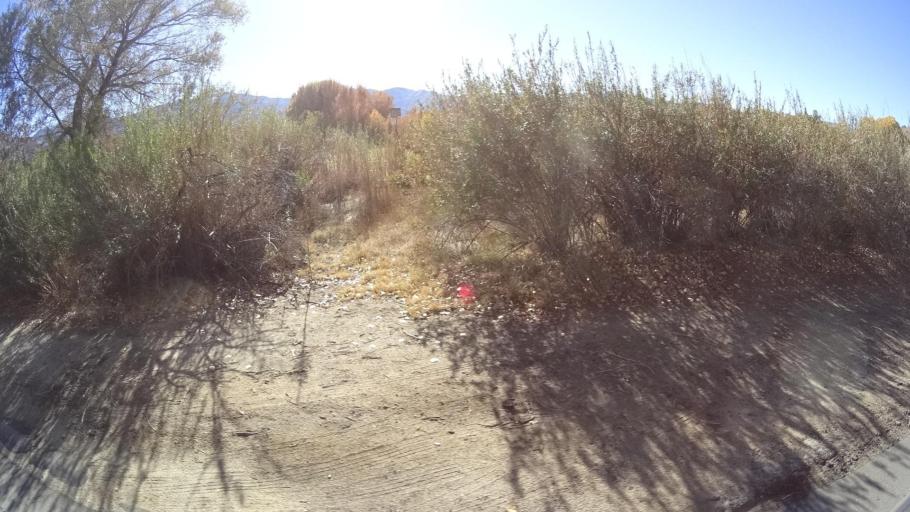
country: US
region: California
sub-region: Kern County
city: Weldon
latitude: 35.6708
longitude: -118.3247
